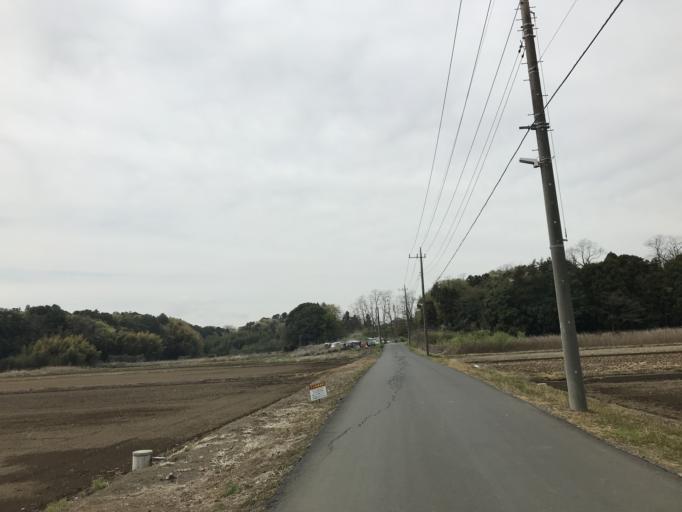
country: JP
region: Ibaraki
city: Moriya
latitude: 35.9486
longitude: 140.0113
